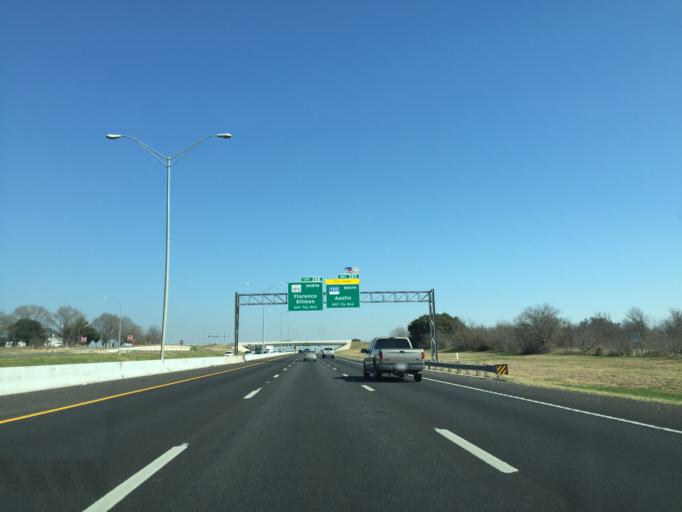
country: US
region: Texas
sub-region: Williamson County
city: Serenada
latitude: 30.6705
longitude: -97.6664
